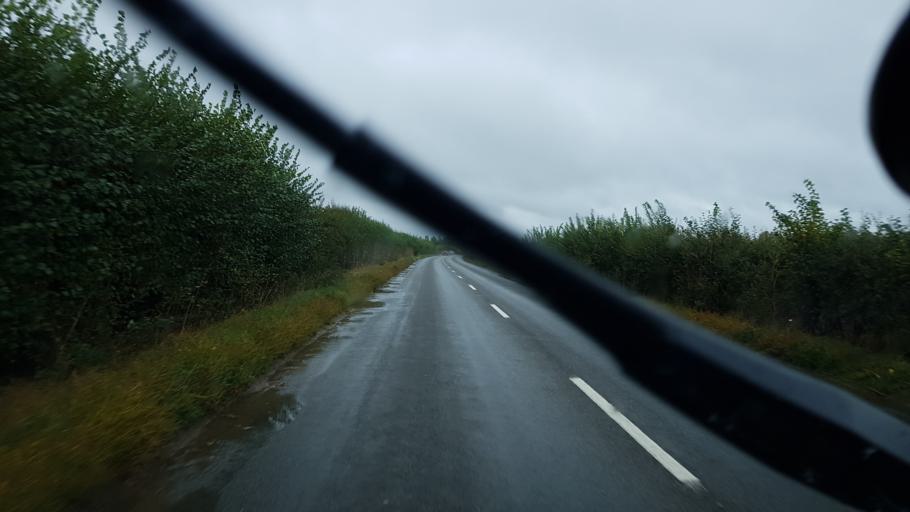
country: GB
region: England
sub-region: Oxfordshire
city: Frilford
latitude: 51.6758
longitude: -1.3931
